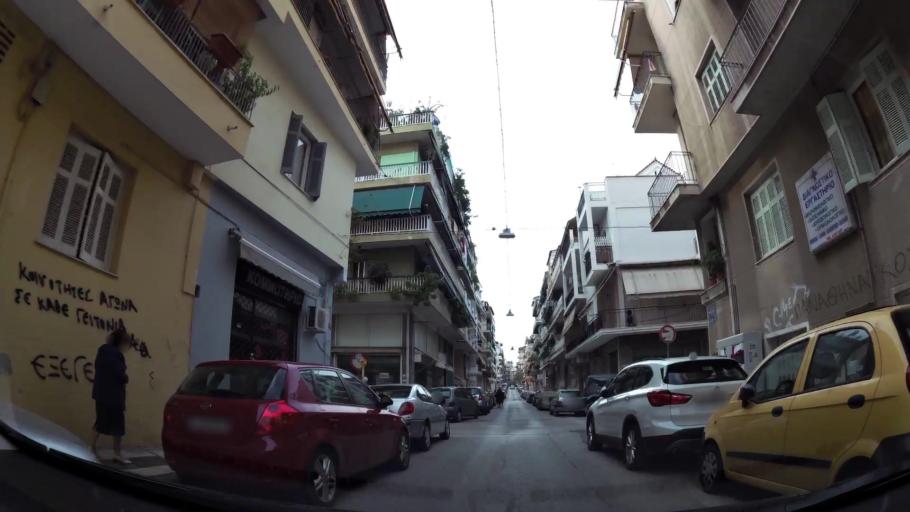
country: GR
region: Attica
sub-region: Nomarchia Athinas
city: Kipseli
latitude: 38.0059
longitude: 23.7247
